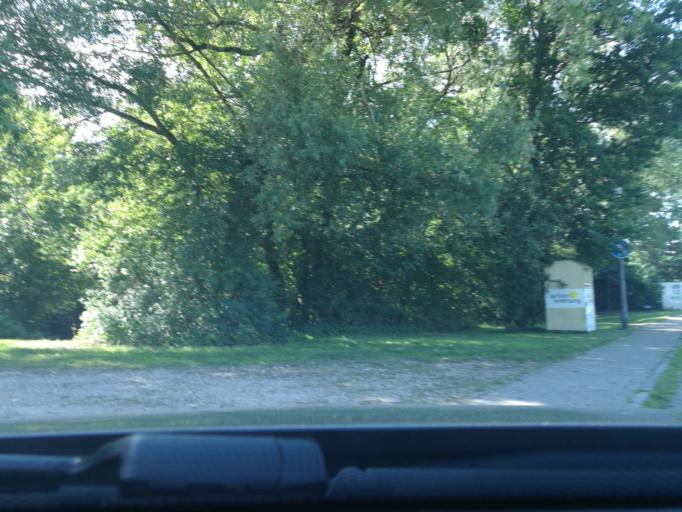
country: DE
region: Bavaria
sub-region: Regierungsbezirk Mittelfranken
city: Schwarzenbruck
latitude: 49.3548
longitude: 11.2338
